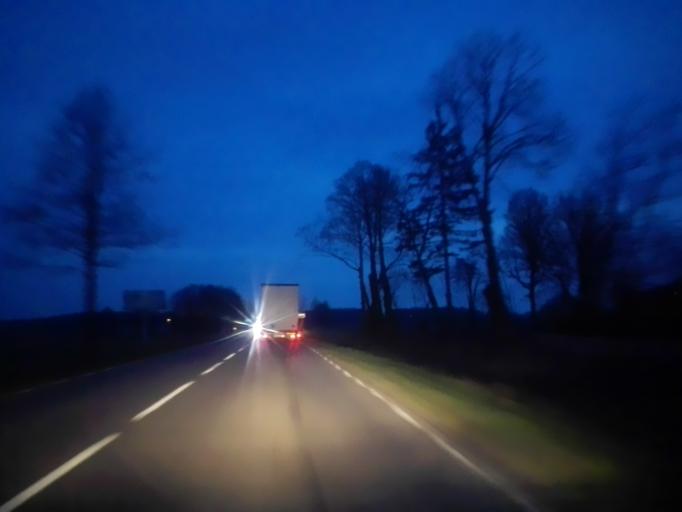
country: PL
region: Podlasie
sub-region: Powiat lomzynski
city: Sniadowo
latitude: 53.0361
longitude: 21.9806
